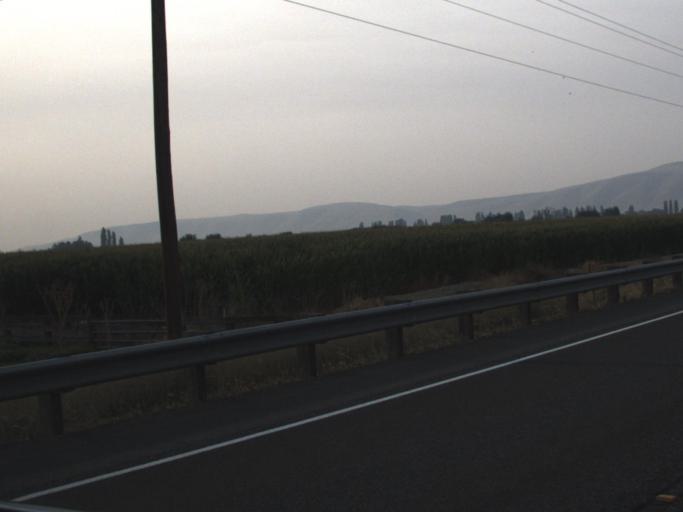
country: US
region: Washington
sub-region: Yakima County
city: Toppenish
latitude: 46.3524
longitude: -120.3205
